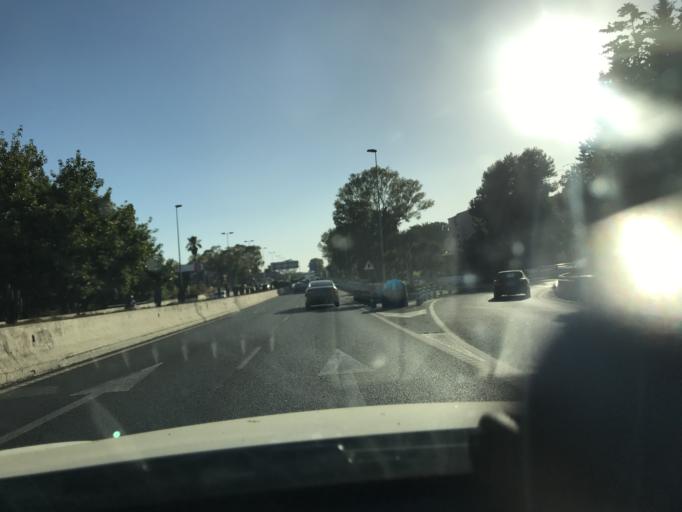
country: ES
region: Andalusia
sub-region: Provincia de Malaga
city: Marbella
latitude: 36.4878
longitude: -4.9633
